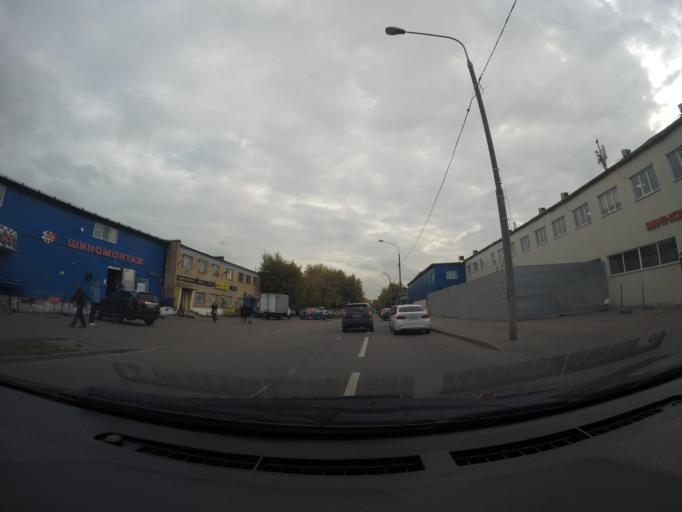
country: RU
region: Moscow
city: Lefortovo
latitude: 55.7592
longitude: 37.7331
